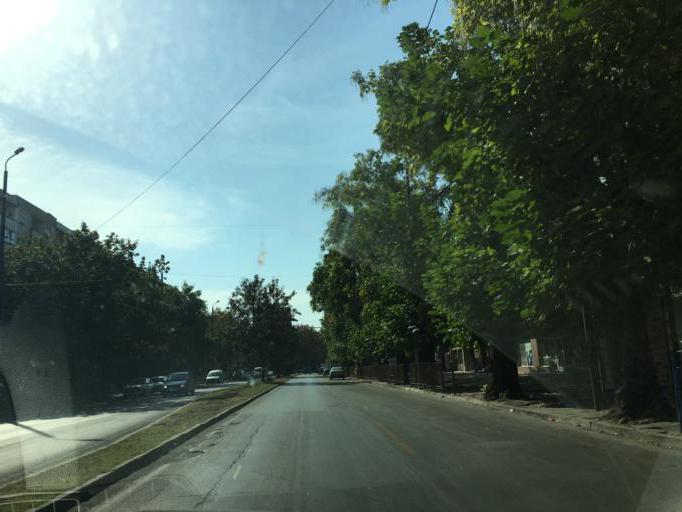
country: BG
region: Pazardzhik
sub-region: Obshtina Pazardzhik
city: Pazardzhik
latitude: 42.2026
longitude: 24.3313
